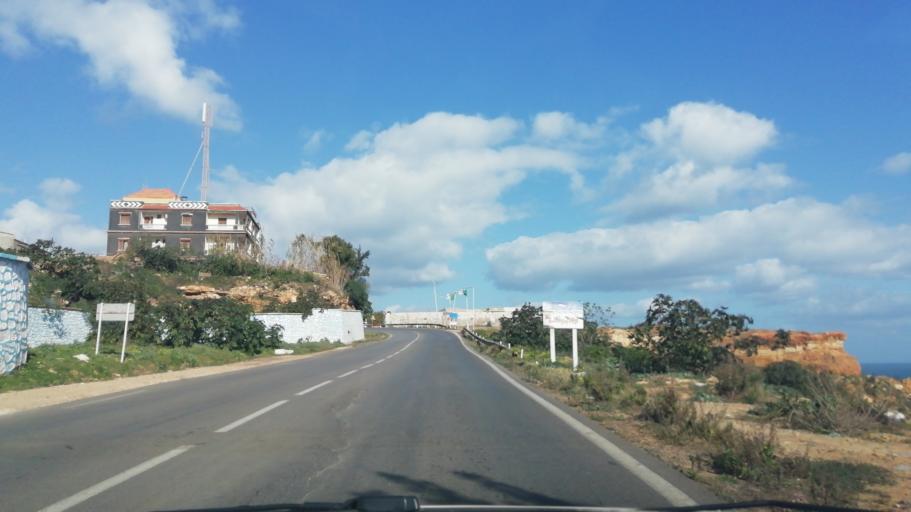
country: DZ
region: Relizane
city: Mazouna
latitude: 36.3224
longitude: 0.6789
